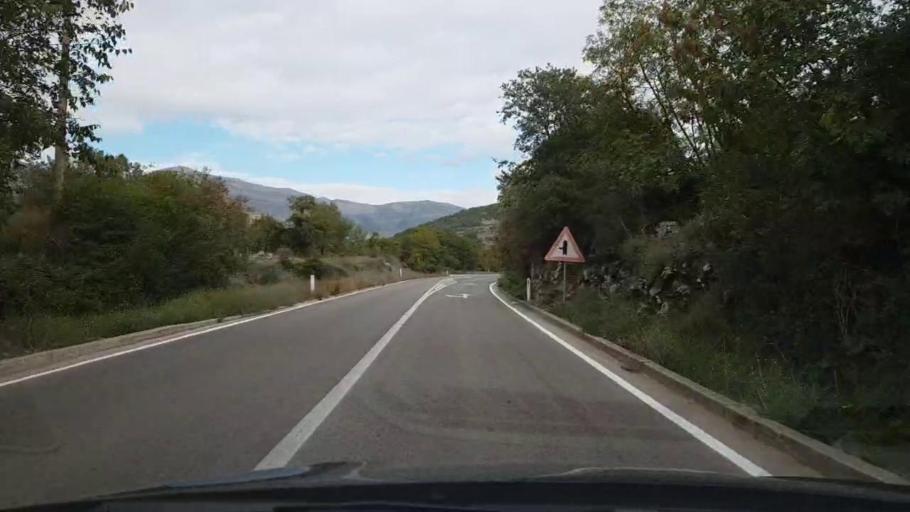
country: BA
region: Republika Srpska
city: Trebinje
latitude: 42.6838
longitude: 18.3044
